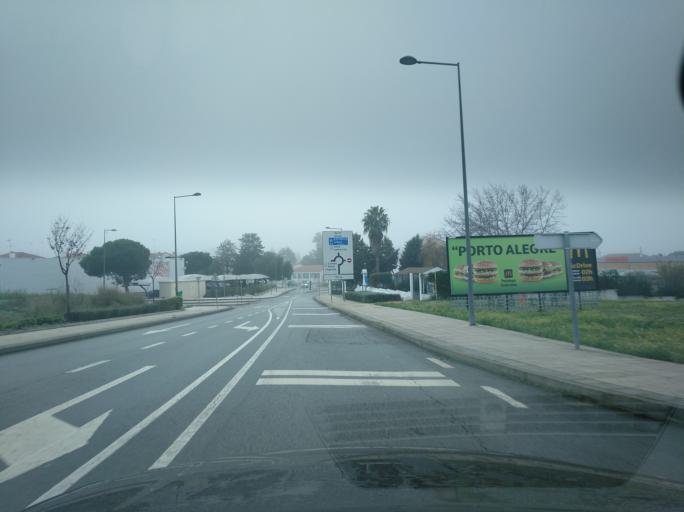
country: PT
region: Portalegre
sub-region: Campo Maior
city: Campo Maior
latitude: 39.0168
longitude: -7.0745
